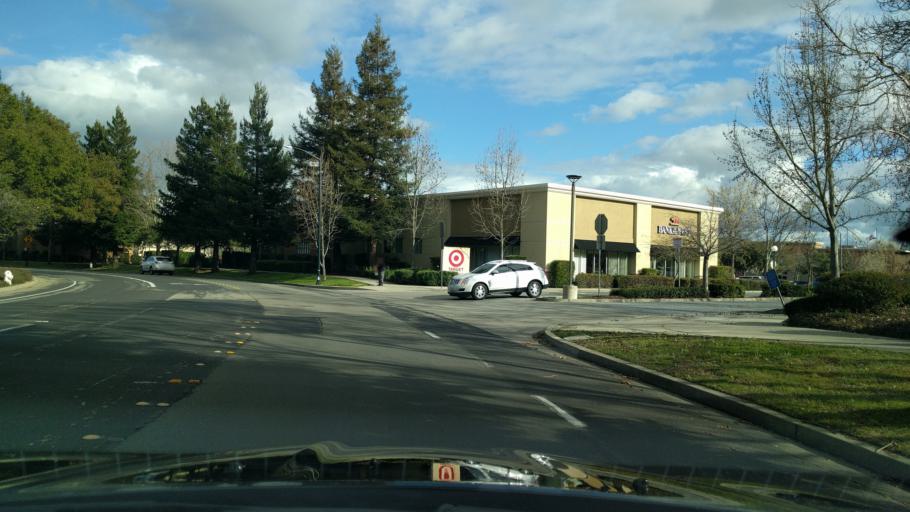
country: US
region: California
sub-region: Contra Costa County
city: San Ramon
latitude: 37.7630
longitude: -121.9634
